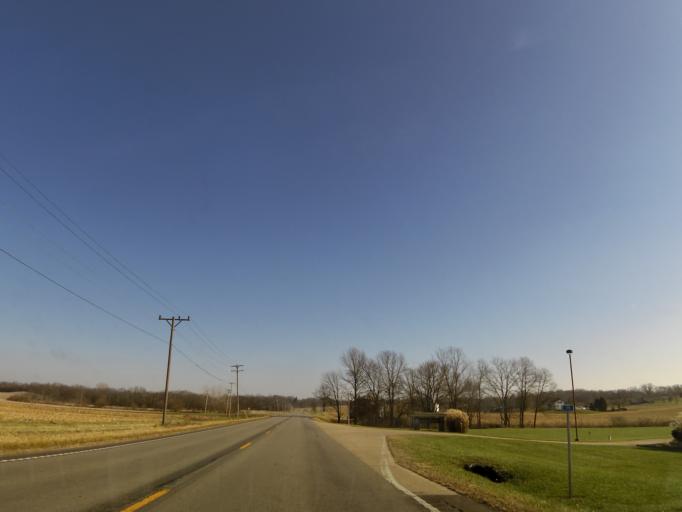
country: US
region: Indiana
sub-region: Fayette County
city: Connersville
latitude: 39.6389
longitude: -85.0796
